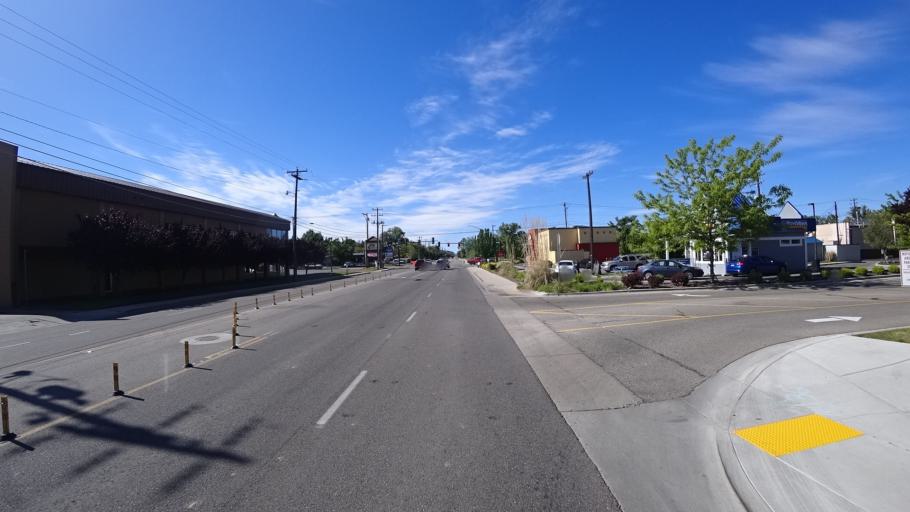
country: US
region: Idaho
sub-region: Ada County
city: Garden City
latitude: 43.6035
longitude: -116.2436
